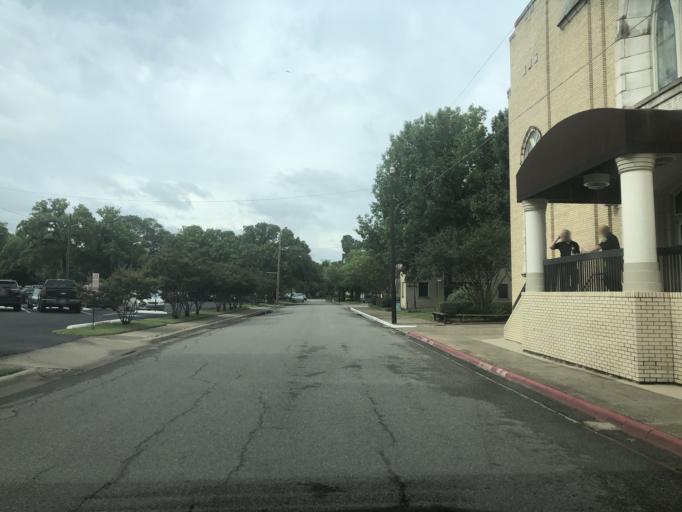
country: US
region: Texas
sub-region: Dallas County
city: Irving
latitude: 32.8104
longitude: -96.9462
